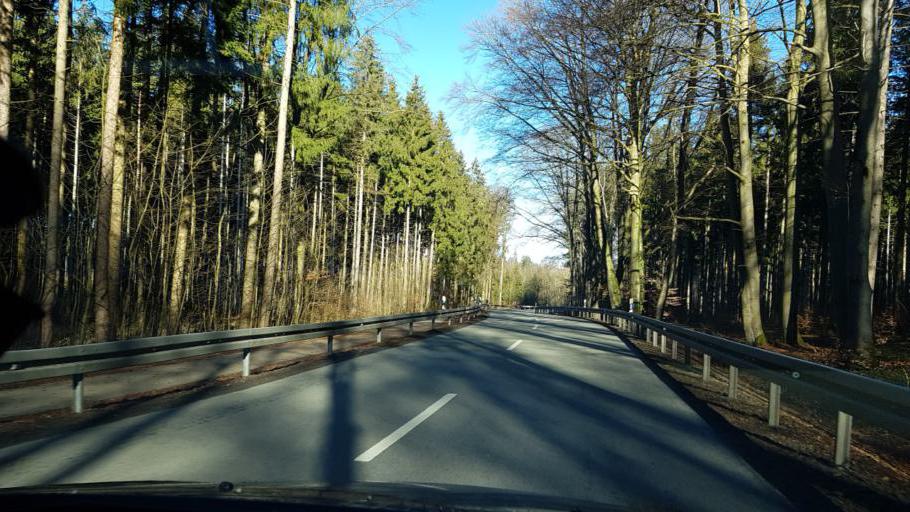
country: DE
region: Bavaria
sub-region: Upper Bavaria
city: Oberschweinbach
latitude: 48.2278
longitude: 11.1706
